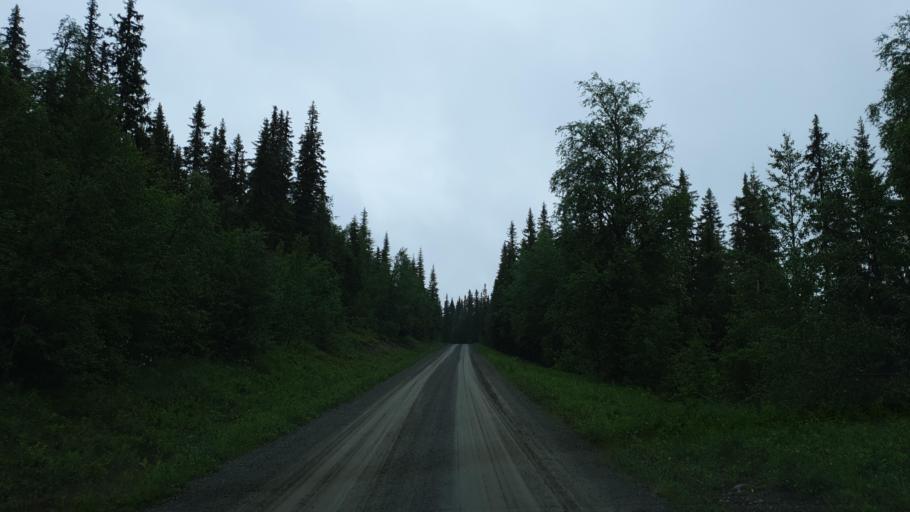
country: SE
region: Vaesterbotten
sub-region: Vilhelmina Kommun
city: Sjoberg
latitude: 65.3320
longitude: 15.9059
